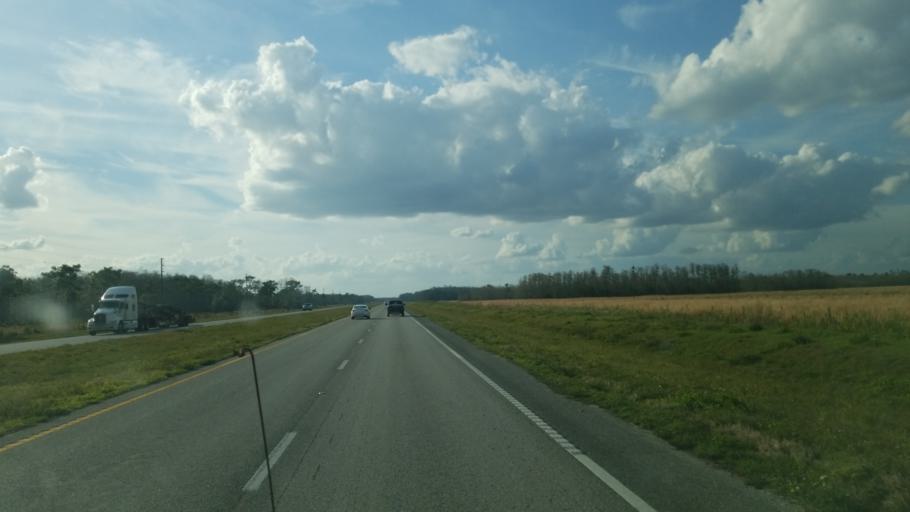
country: US
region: Florida
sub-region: Osceola County
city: Saint Cloud
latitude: 28.1392
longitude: -81.0443
